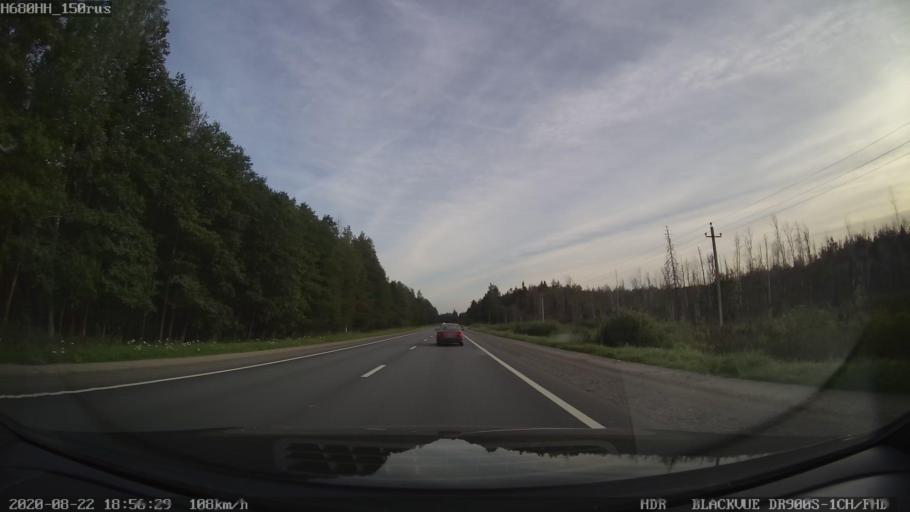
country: RU
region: Tverskaya
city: Rameshki
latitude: 57.1826
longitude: 36.0816
